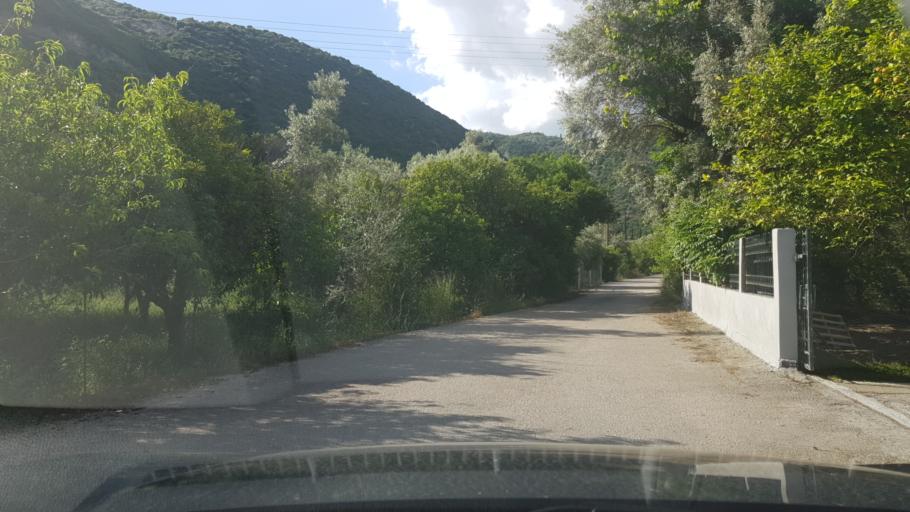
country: GR
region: Ionian Islands
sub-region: Lefkada
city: Nidri
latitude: 38.7162
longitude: 20.6957
